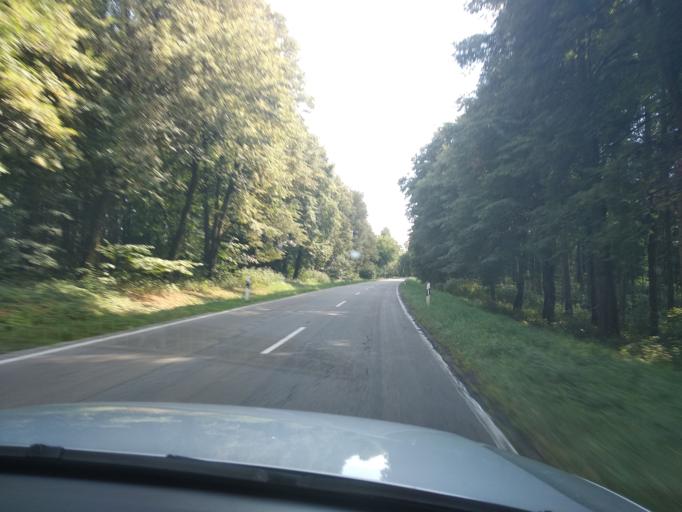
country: DE
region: Baden-Wuerttemberg
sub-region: Tuebingen Region
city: Leutkirch im Allgau
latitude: 47.8717
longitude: 9.9941
